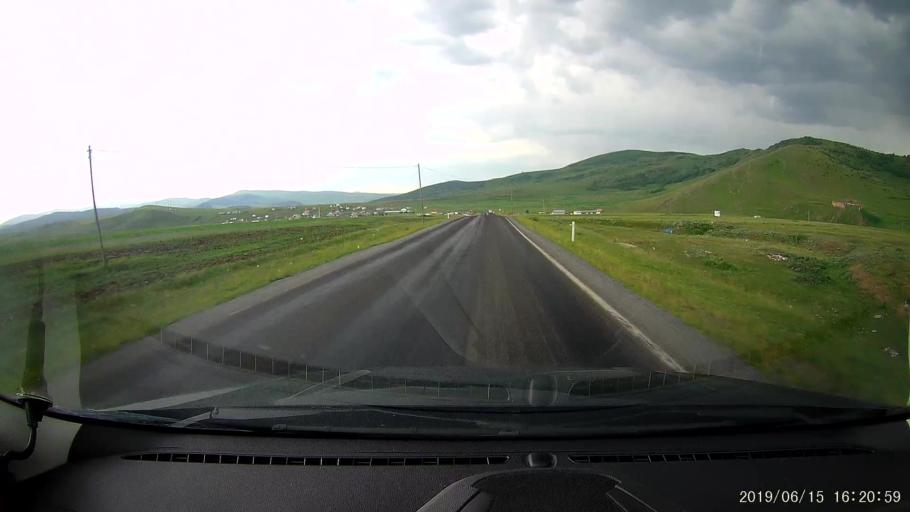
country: TR
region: Ardahan
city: Hanak
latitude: 41.2047
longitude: 42.8464
